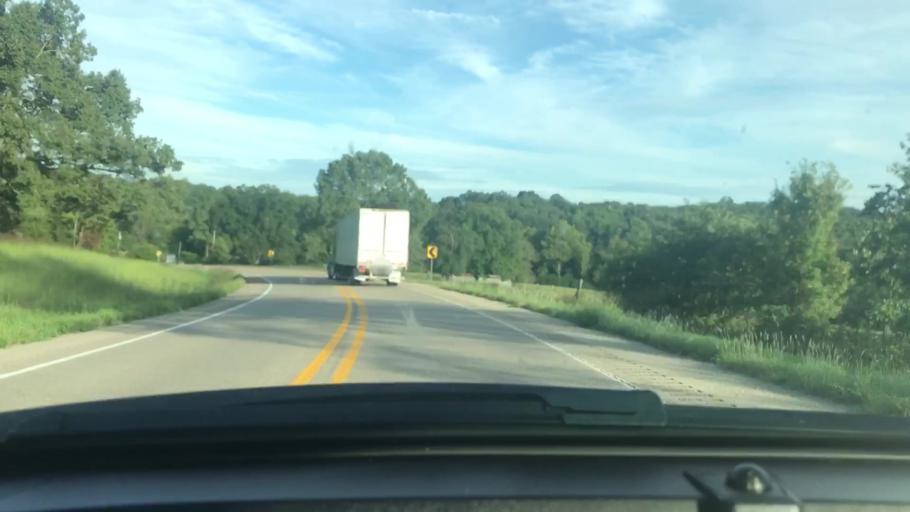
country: US
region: Arkansas
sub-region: Randolph County
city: Pocahontas
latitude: 36.2127
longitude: -91.2131
